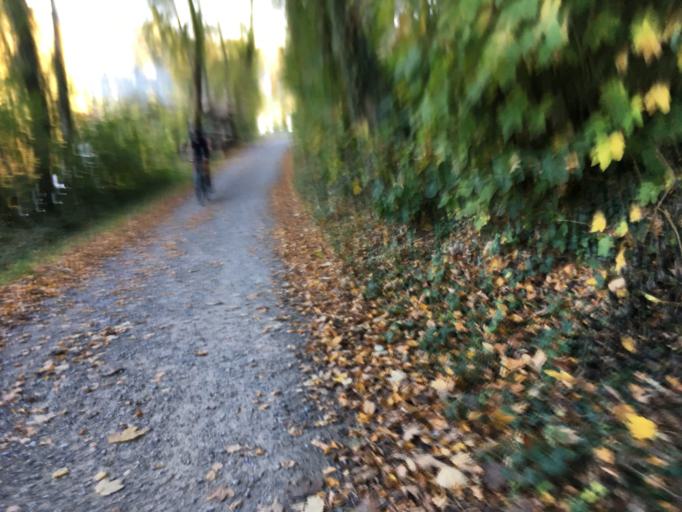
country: CH
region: Zurich
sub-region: Bezirk Buelach
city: Buelach / Soligaenter
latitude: 47.5554
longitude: 8.5506
